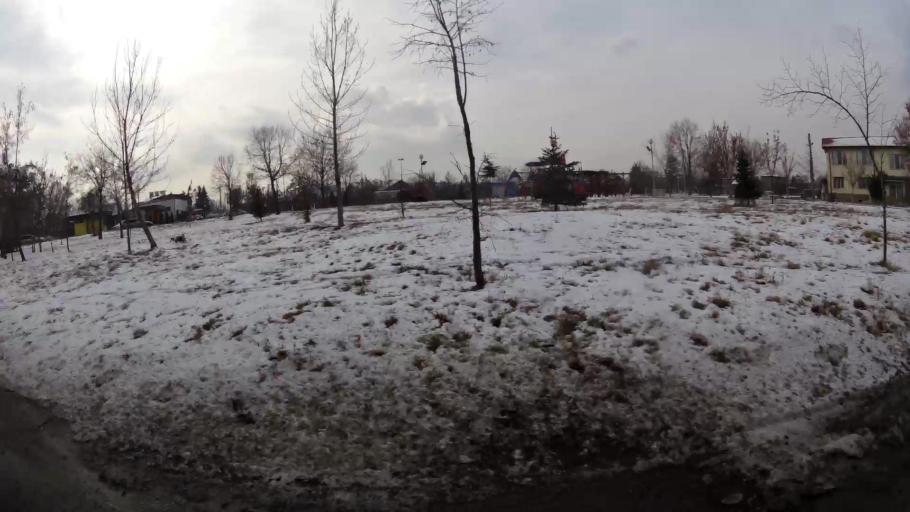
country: BG
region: Sofia-Capital
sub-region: Stolichna Obshtina
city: Sofia
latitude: 42.7124
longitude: 23.4085
